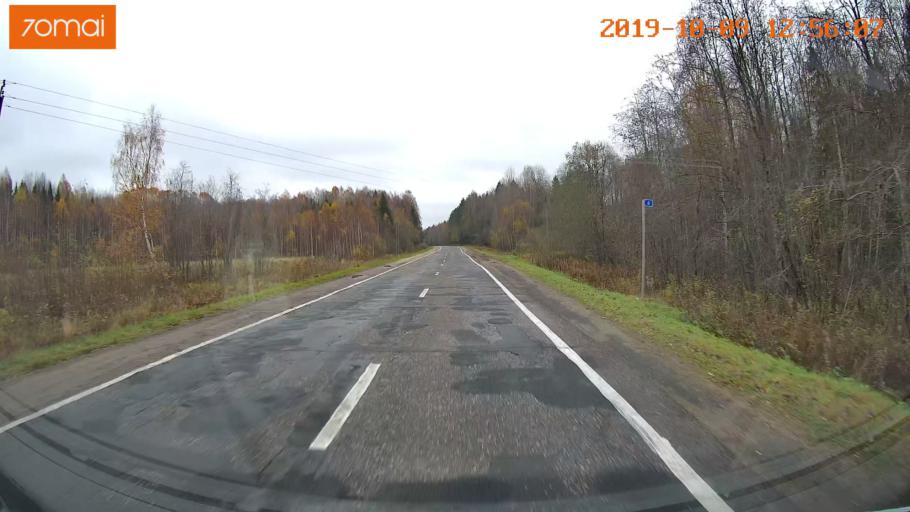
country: RU
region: Jaroslavl
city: Prechistoye
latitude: 58.3958
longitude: 40.4101
